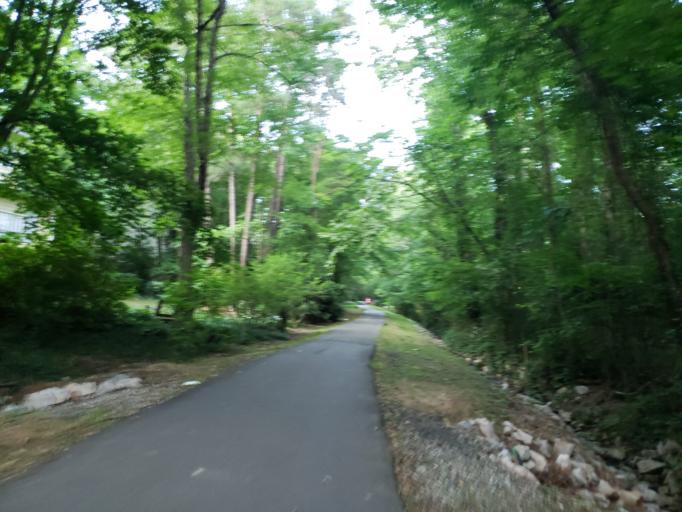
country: US
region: North Carolina
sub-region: Durham County
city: Durham
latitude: 35.9191
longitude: -78.9388
